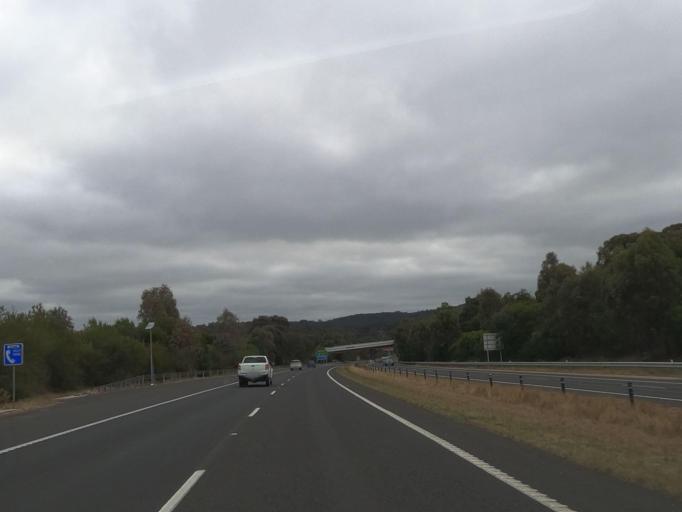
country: AU
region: Victoria
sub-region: Mount Alexander
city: Castlemaine
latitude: -37.0120
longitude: 144.2533
